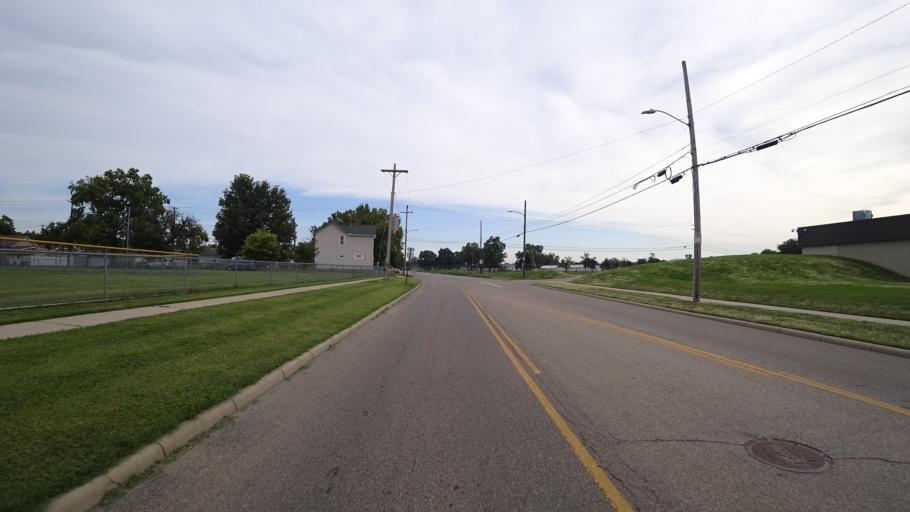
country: US
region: Ohio
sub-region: Butler County
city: Hamilton
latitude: 39.3981
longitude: -84.5412
